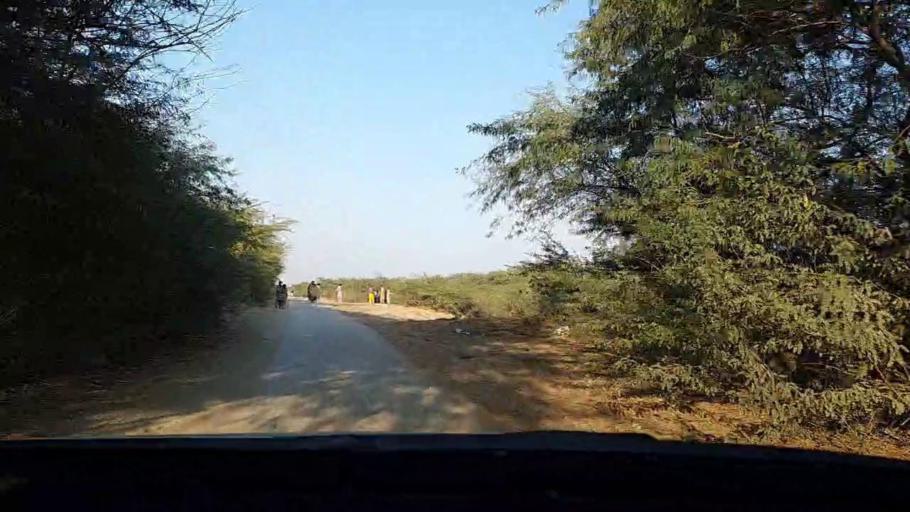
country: PK
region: Sindh
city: Tando Mittha Khan
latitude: 25.8661
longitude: 69.3072
